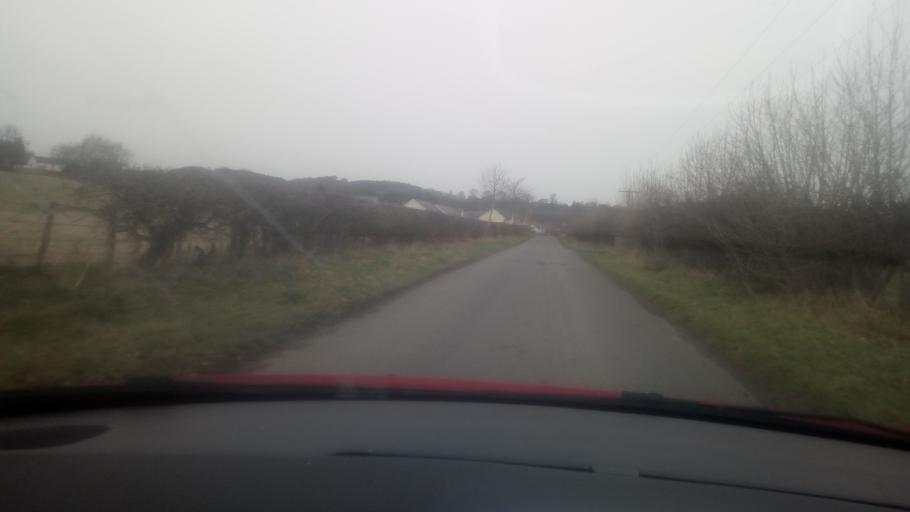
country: GB
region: Scotland
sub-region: The Scottish Borders
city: Jedburgh
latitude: 55.5098
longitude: -2.5903
